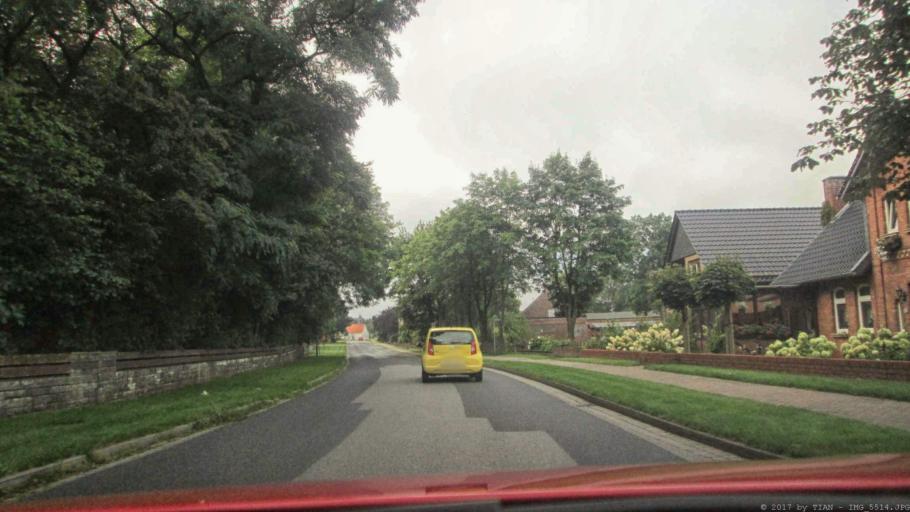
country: DE
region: Lower Saxony
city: Tulau
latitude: 52.6234
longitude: 10.8142
